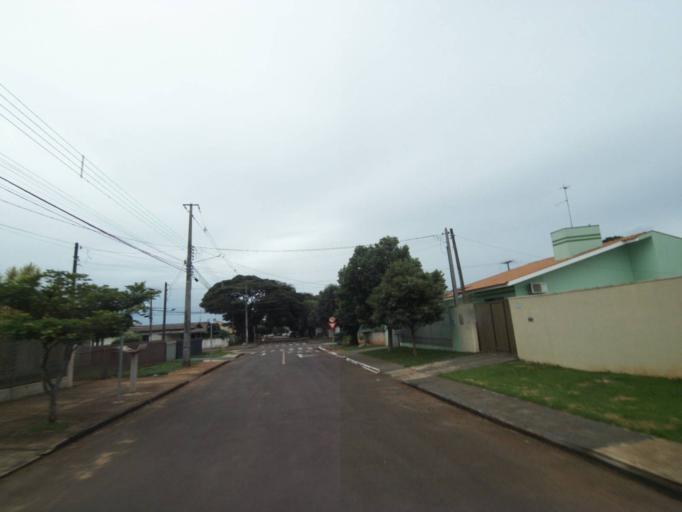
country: BR
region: Parana
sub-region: Campo Mourao
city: Campo Mourao
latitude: -24.0258
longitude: -52.3633
